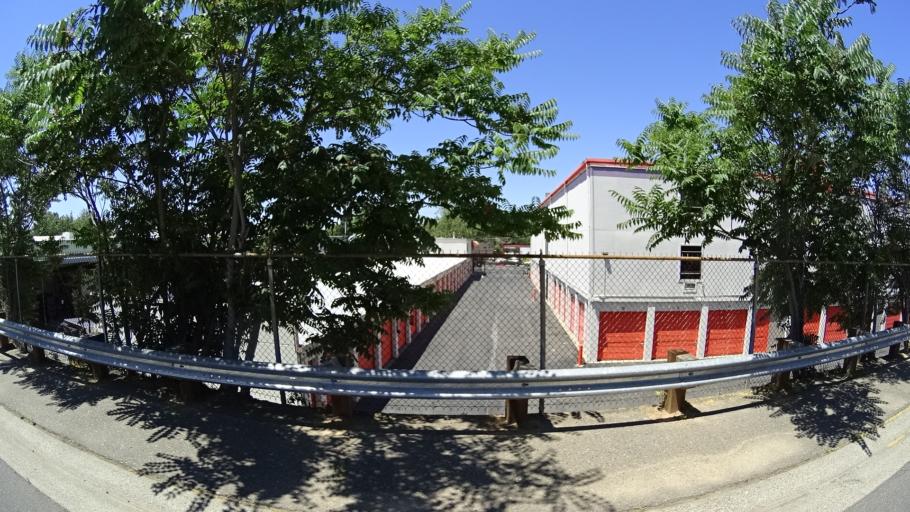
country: US
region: California
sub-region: Sacramento County
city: Sacramento
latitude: 38.5666
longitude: -121.4320
